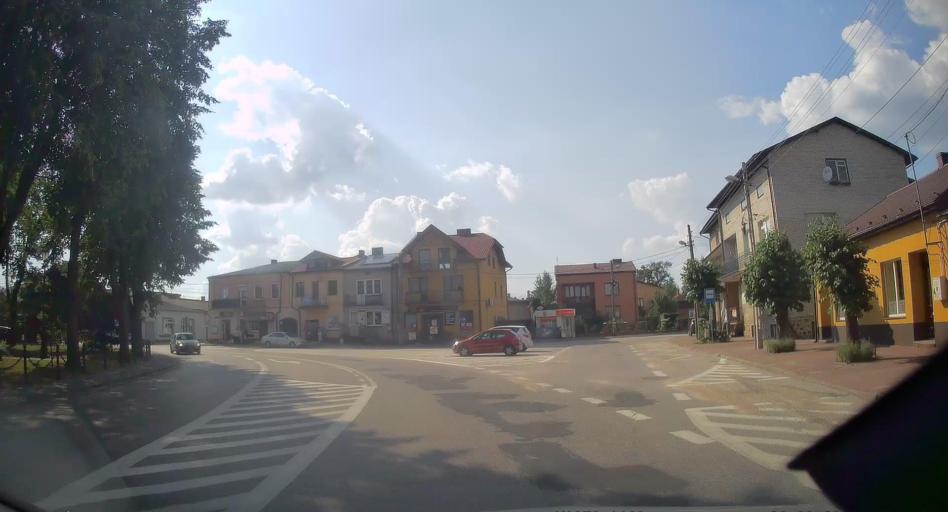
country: PL
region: Swietokrzyskie
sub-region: Powiat konecki
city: Radoszyce
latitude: 51.0740
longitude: 20.2597
